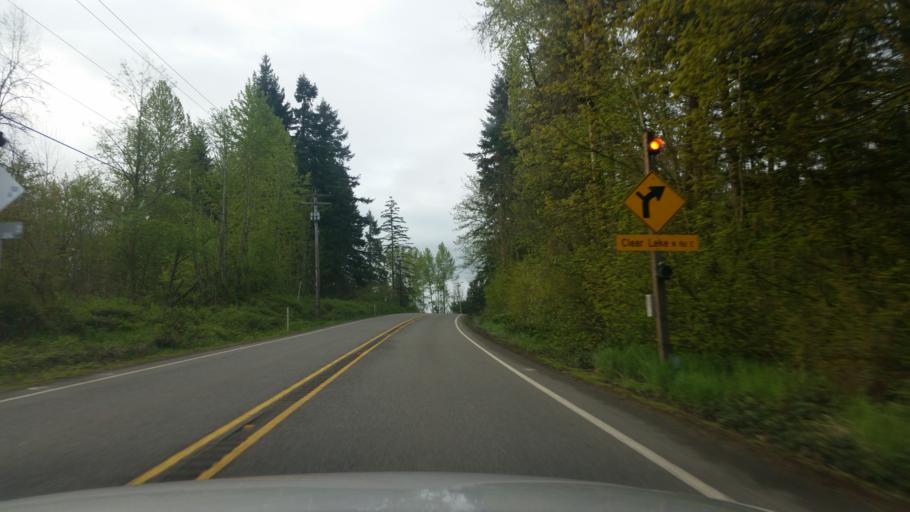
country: US
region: Washington
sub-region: Pierce County
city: Eatonville
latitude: 46.9242
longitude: -122.2832
